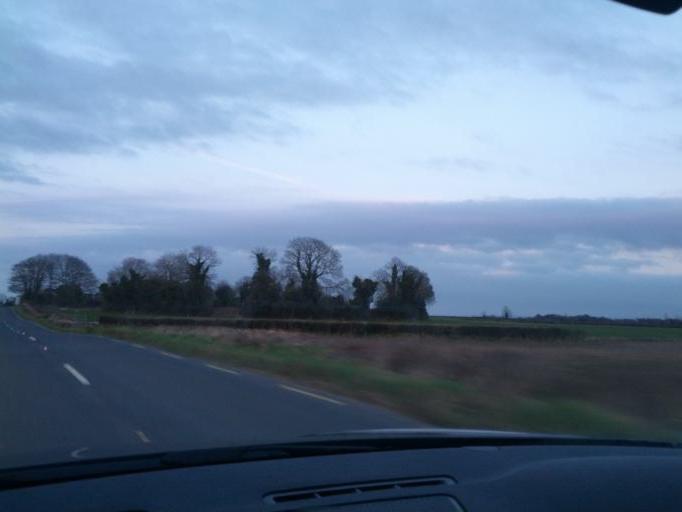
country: IE
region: Leinster
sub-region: Uibh Fhaili
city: Banagher
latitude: 53.0934
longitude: -8.0354
